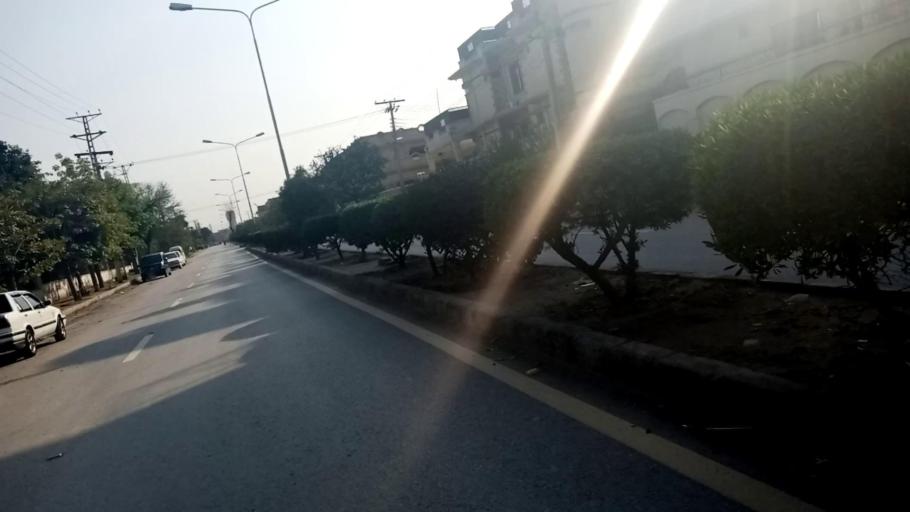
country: PK
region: Khyber Pakhtunkhwa
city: Peshawar
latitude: 33.9922
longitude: 71.4459
